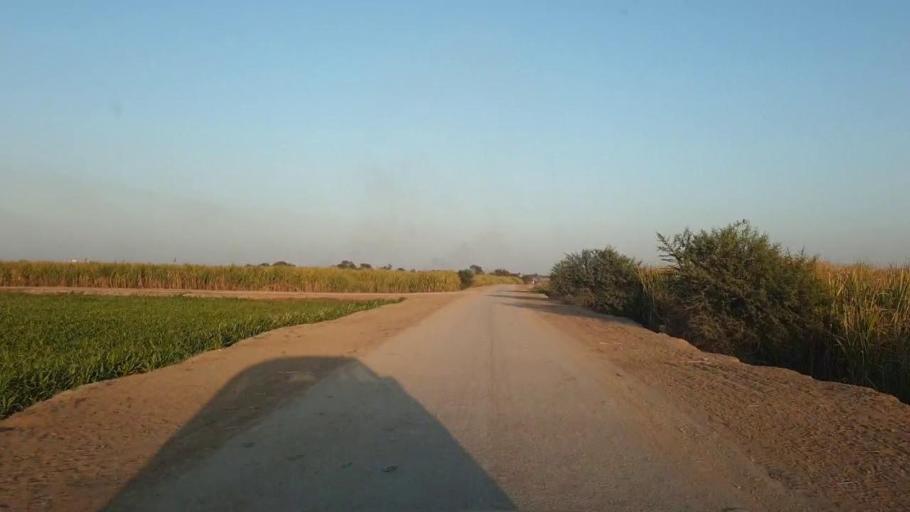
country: PK
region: Sindh
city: Chambar
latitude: 25.3712
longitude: 68.7572
